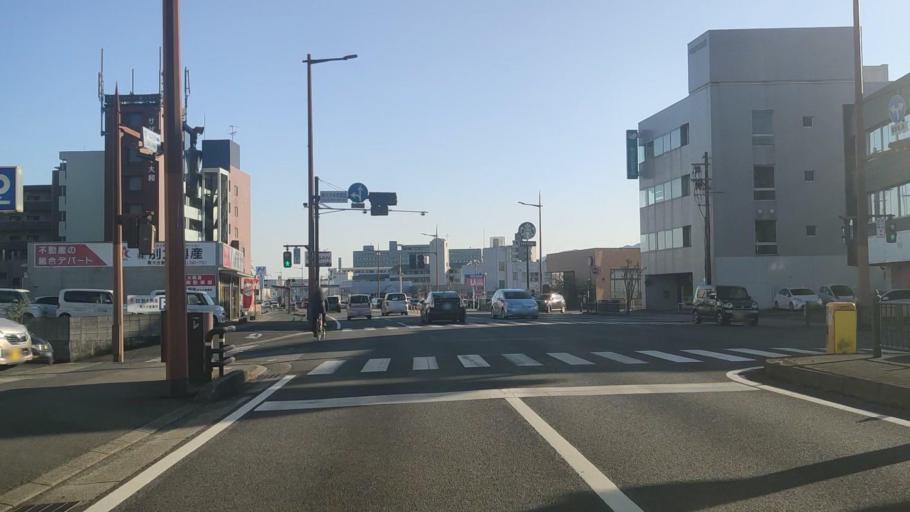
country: JP
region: Oita
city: Oita
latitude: 33.2134
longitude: 131.5964
